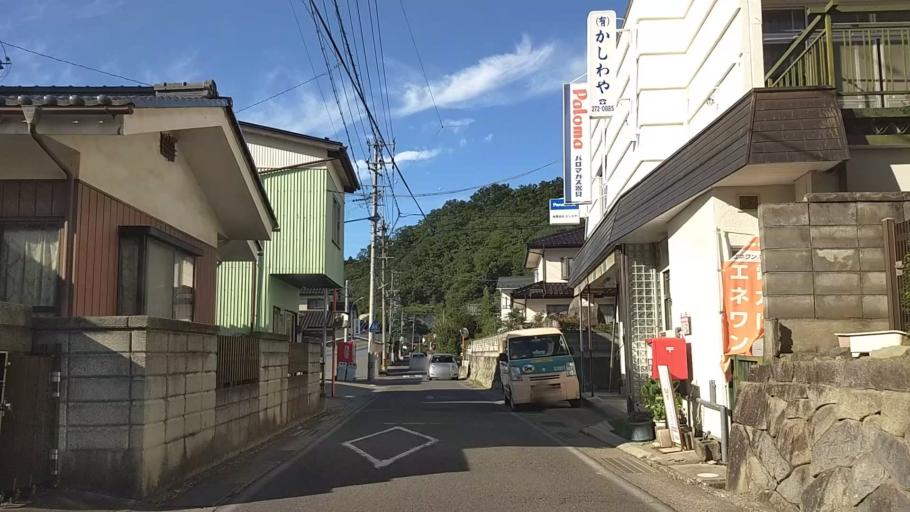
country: JP
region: Nagano
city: Nagano-shi
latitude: 36.5542
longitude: 138.1564
